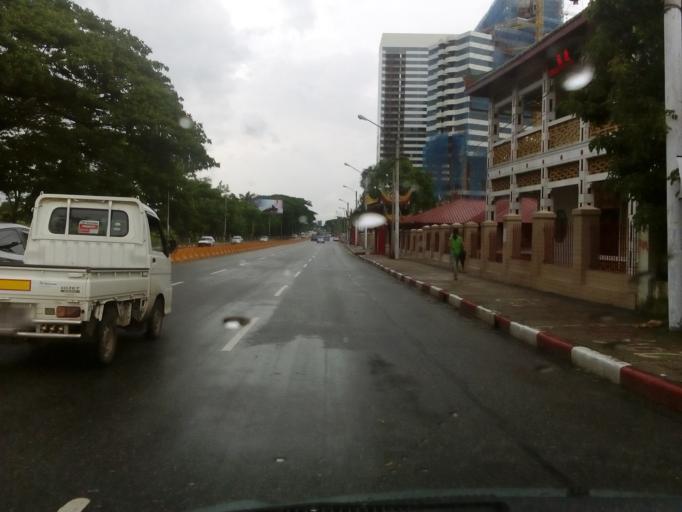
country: MM
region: Yangon
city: Yangon
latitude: 16.8243
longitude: 96.1540
